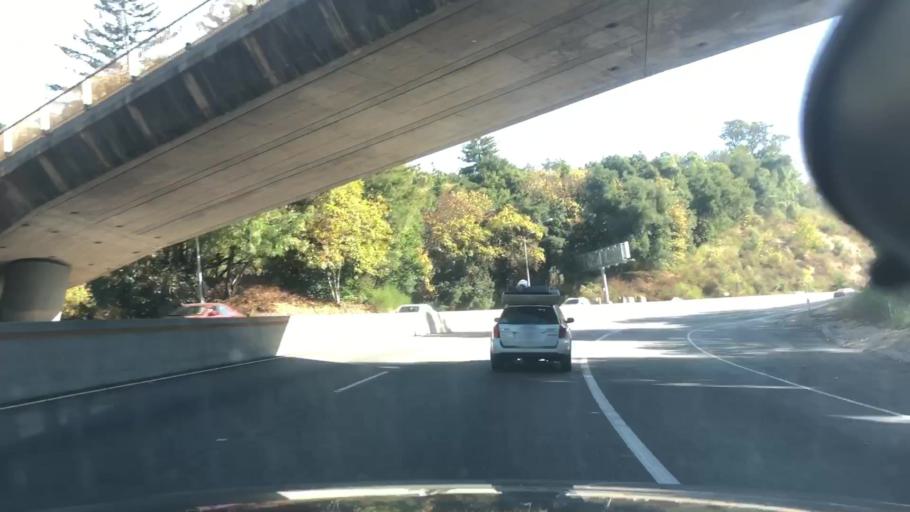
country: US
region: California
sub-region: Santa Clara County
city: Lexington Hills
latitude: 37.1457
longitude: -121.9851
